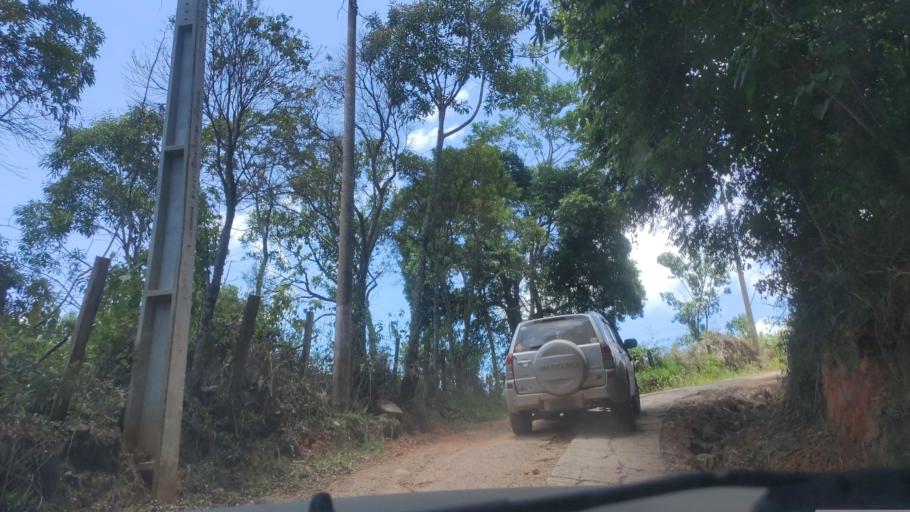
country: BR
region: Minas Gerais
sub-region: Cambui
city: Cambui
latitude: -22.6764
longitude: -45.9675
